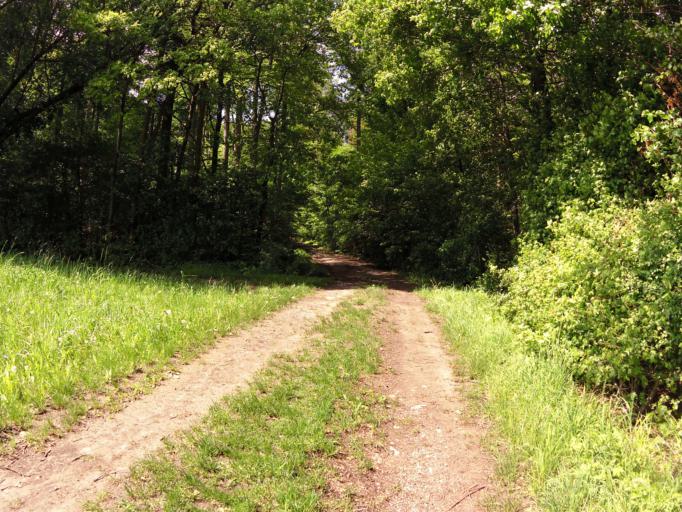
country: DE
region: Bavaria
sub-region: Regierungsbezirk Unterfranken
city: Reichenberg
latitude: 49.7420
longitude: 9.9031
